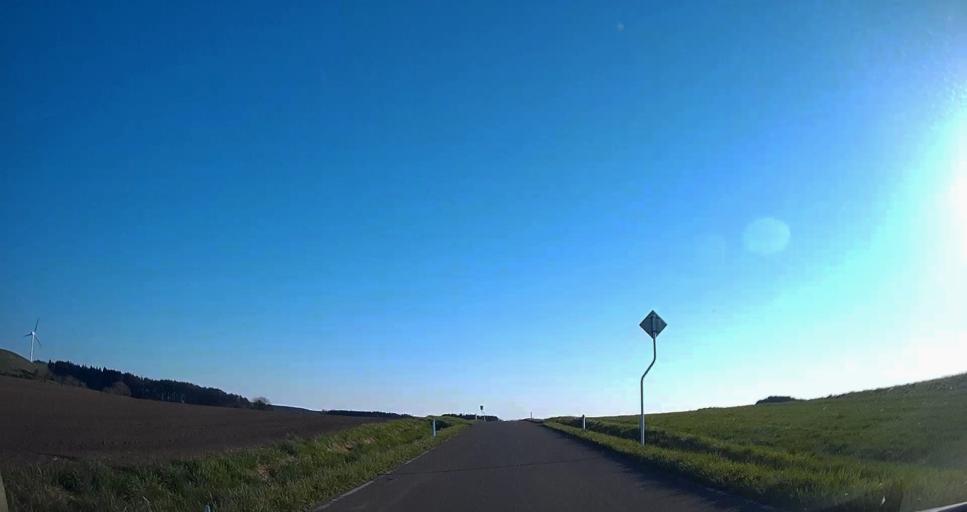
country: JP
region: Aomori
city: Mutsu
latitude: 41.1193
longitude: 141.2777
